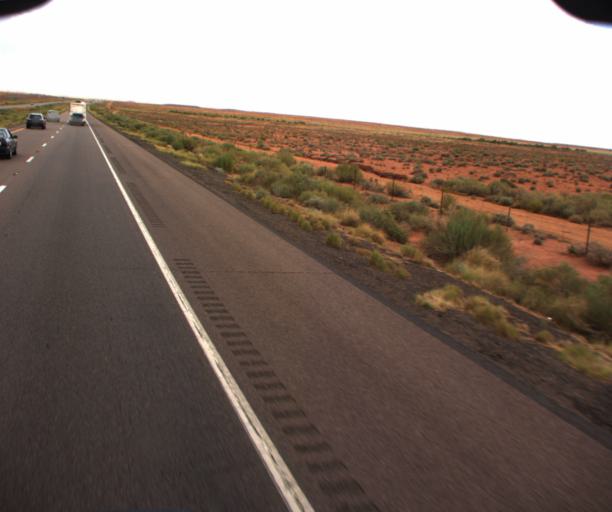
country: US
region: Arizona
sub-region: Coconino County
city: LeChee
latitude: 35.0796
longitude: -110.8762
